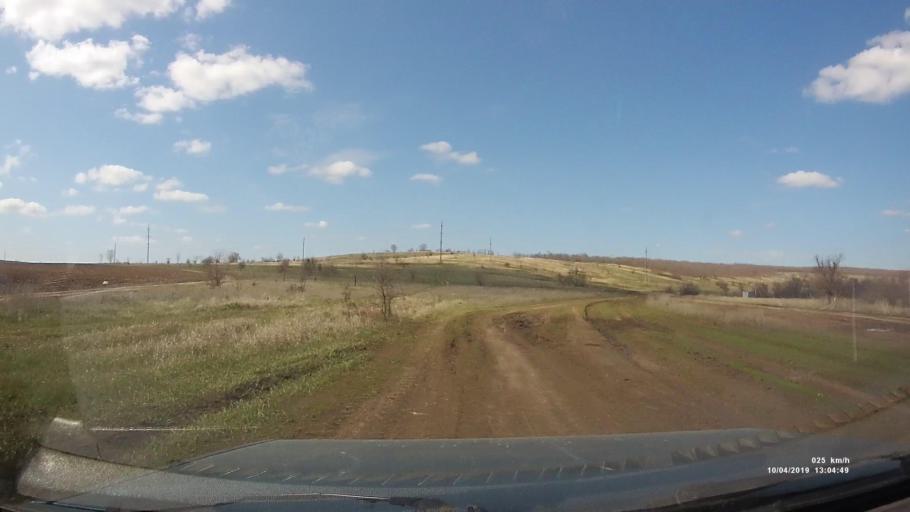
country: RU
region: Rostov
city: Masalovka
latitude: 48.3858
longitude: 40.2348
